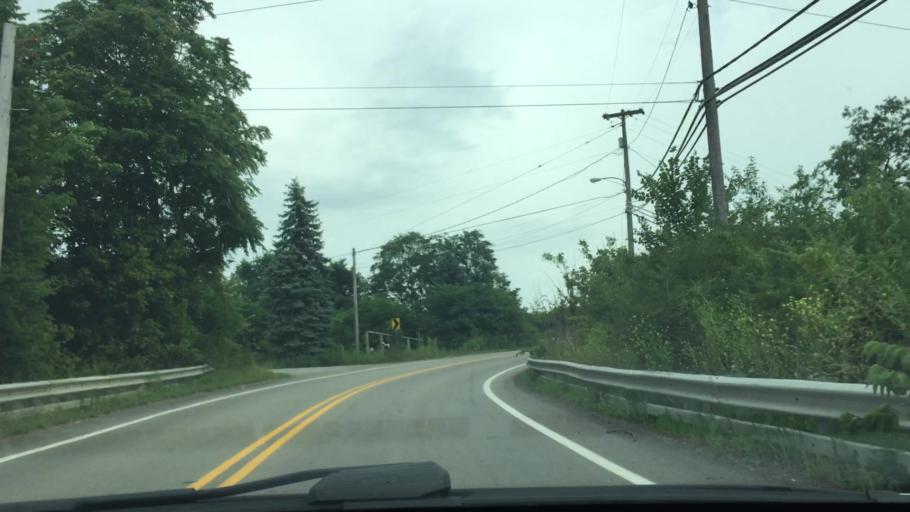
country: US
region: Pennsylvania
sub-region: Allegheny County
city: Bridgeville
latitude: 40.3734
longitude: -80.1137
